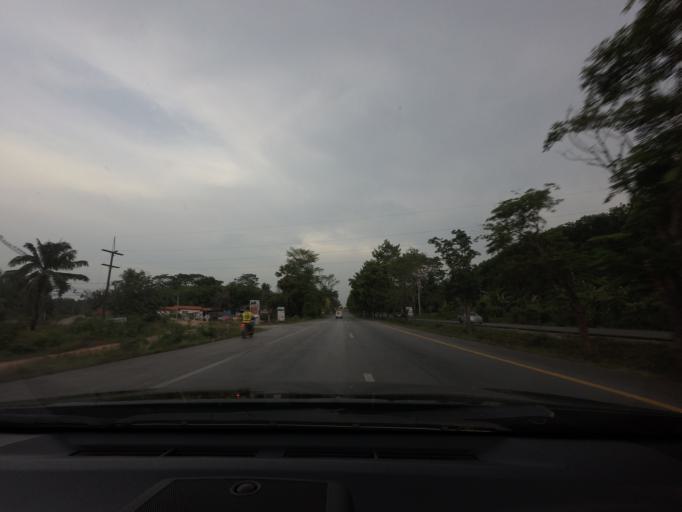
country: TH
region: Surat Thani
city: Tha Chana
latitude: 9.4887
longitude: 99.1387
